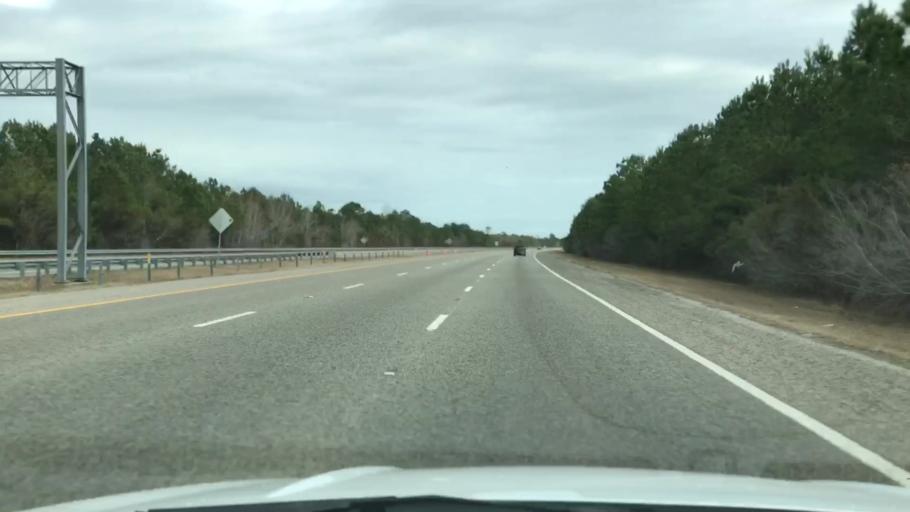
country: US
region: South Carolina
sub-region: Horry County
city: Socastee
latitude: 33.7201
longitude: -78.9974
